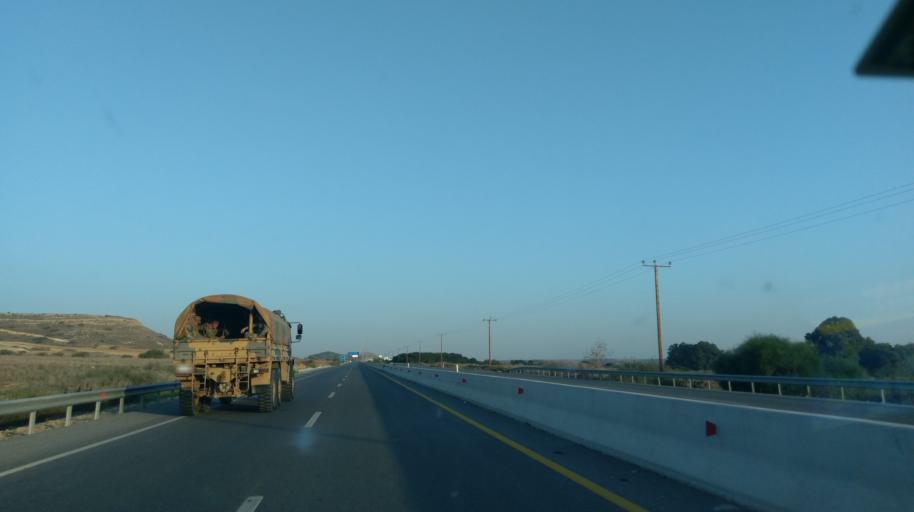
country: CY
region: Lefkosia
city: Akaki
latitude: 35.1957
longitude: 33.1010
